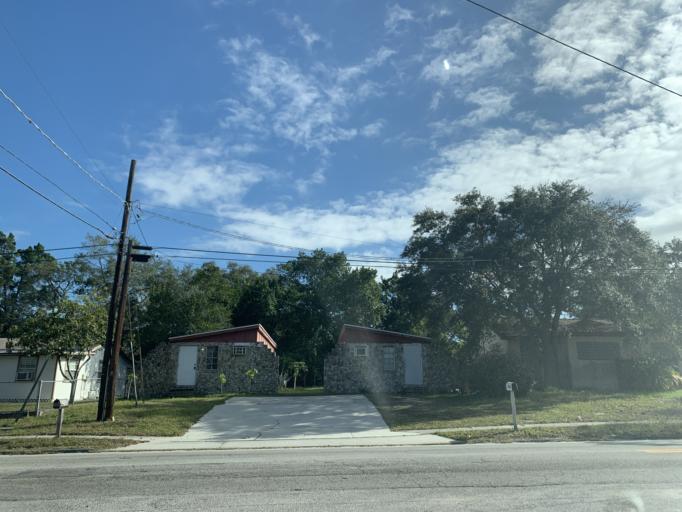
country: US
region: Florida
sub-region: Hillsborough County
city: Temple Terrace
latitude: 28.0390
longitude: -82.4100
